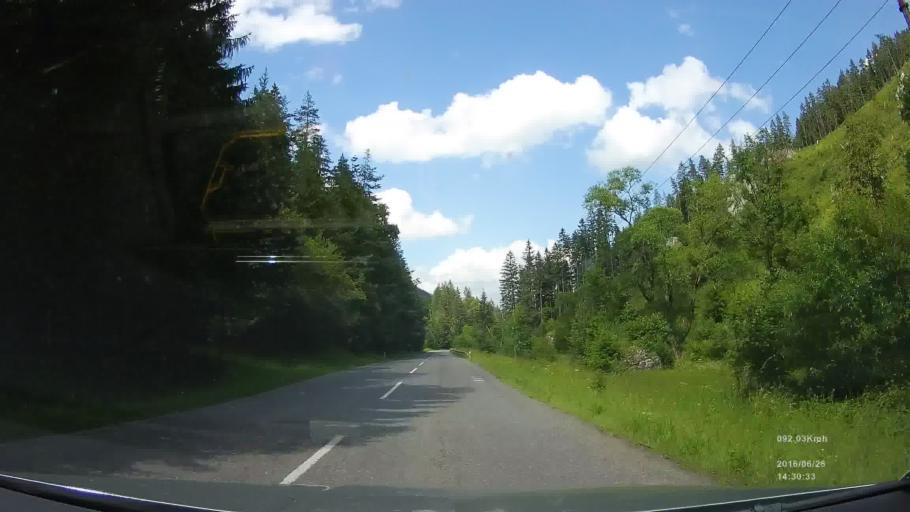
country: SK
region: Zilinsky
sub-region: Okres Zilina
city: Liptovsky Hradok
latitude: 48.9917
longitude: 19.7587
